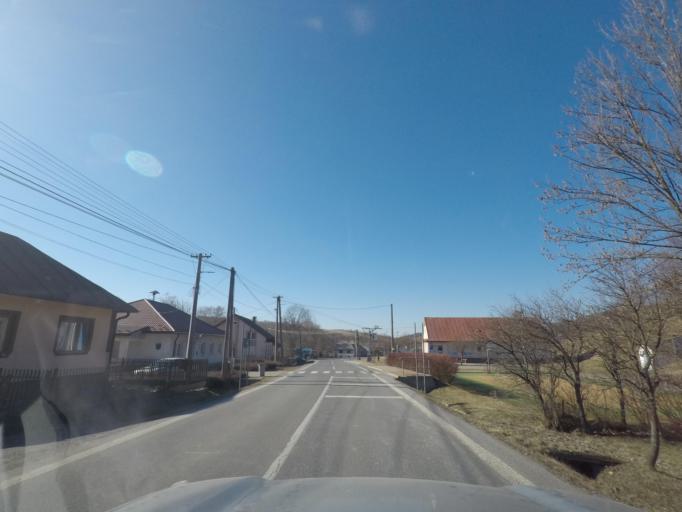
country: SK
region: Presovsky
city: Snina
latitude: 48.9564
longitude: 22.2585
